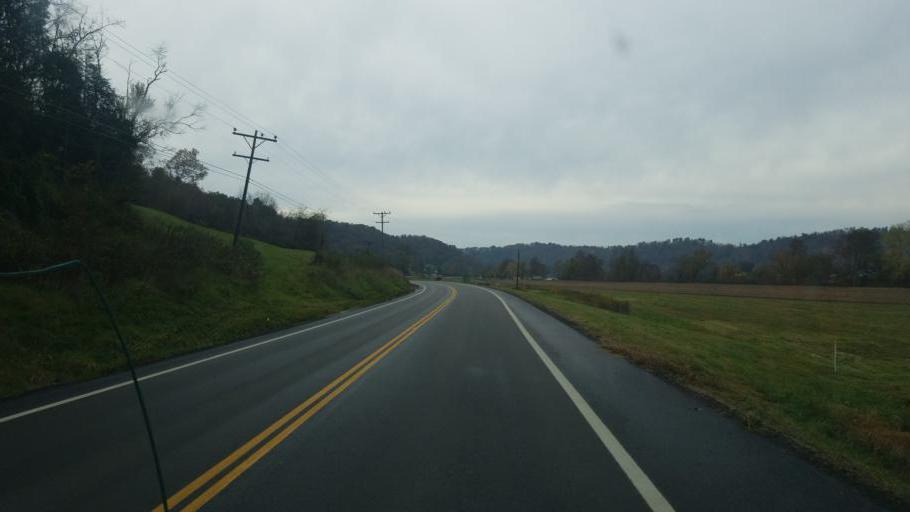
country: US
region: Ohio
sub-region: Washington County
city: Beverly
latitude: 39.5500
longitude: -81.5508
